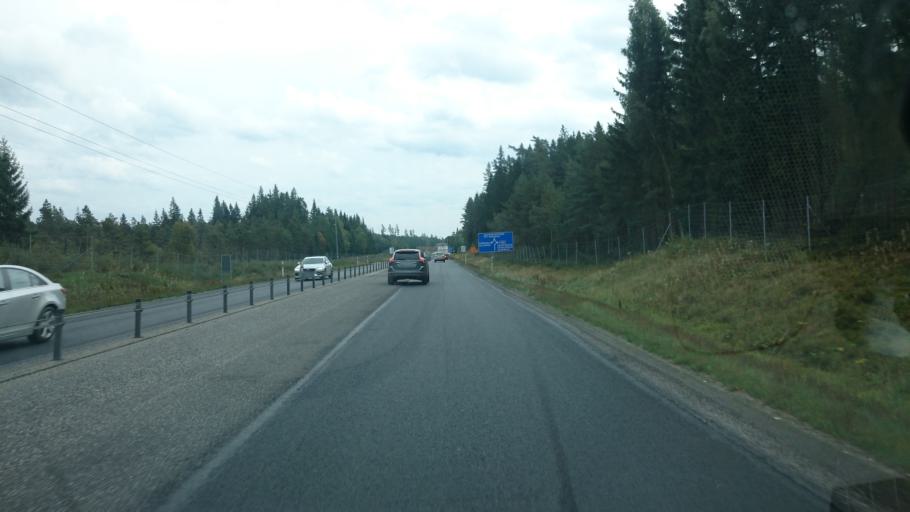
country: SE
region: Vaestra Goetaland
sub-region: Tranemo Kommun
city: Langhem
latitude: 57.6108
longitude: 13.1313
